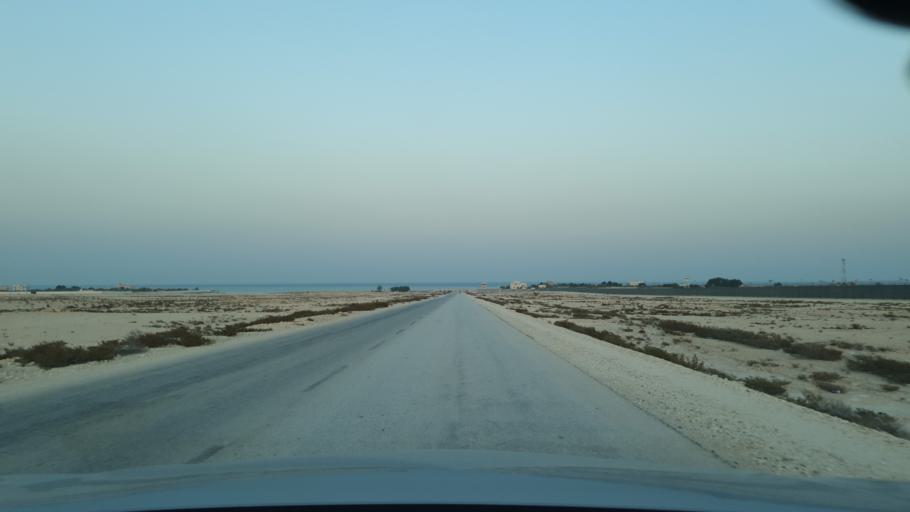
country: BH
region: Central Governorate
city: Dar Kulayb
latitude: 25.9558
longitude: 50.6032
